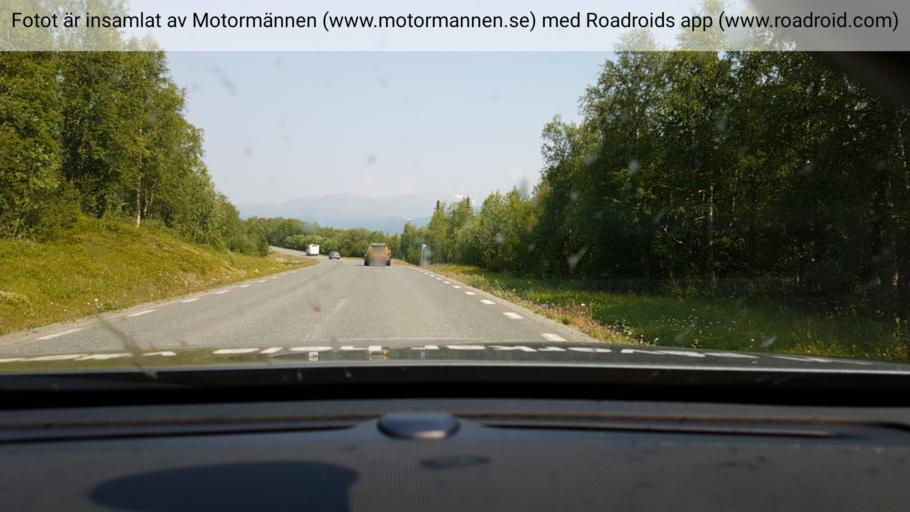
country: NO
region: Nordland
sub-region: Rana
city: Mo i Rana
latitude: 65.7596
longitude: 15.1160
